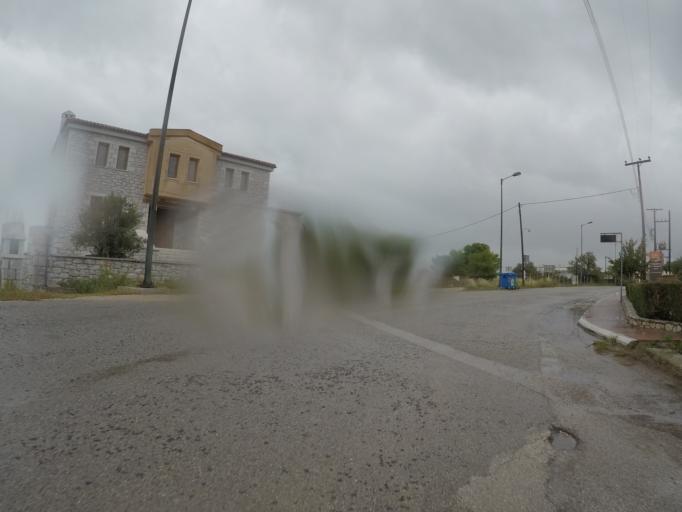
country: GR
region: Peloponnese
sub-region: Nomos Korinthias
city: Arkhaia Korinthos
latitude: 37.9114
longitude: 22.8840
